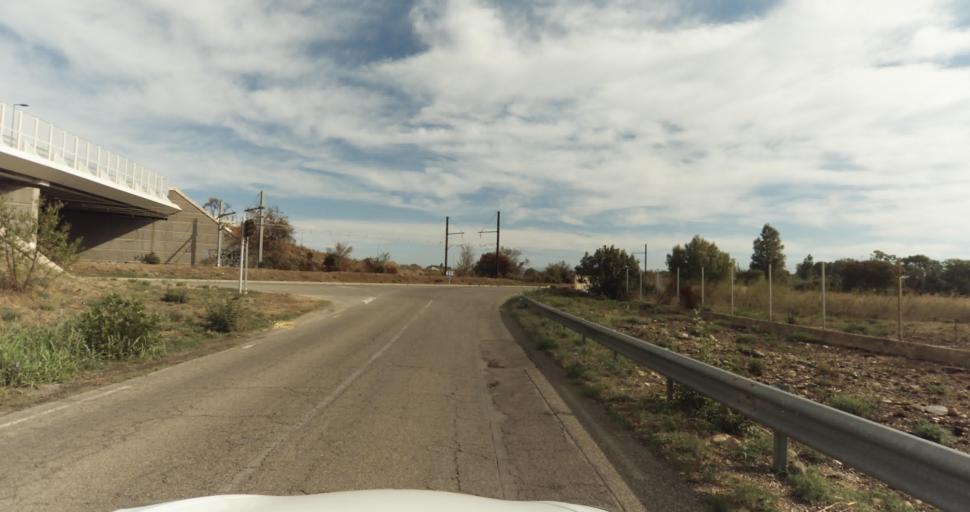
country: FR
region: Provence-Alpes-Cote d'Azur
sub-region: Departement des Bouches-du-Rhone
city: Miramas
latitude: 43.6042
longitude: 5.0087
